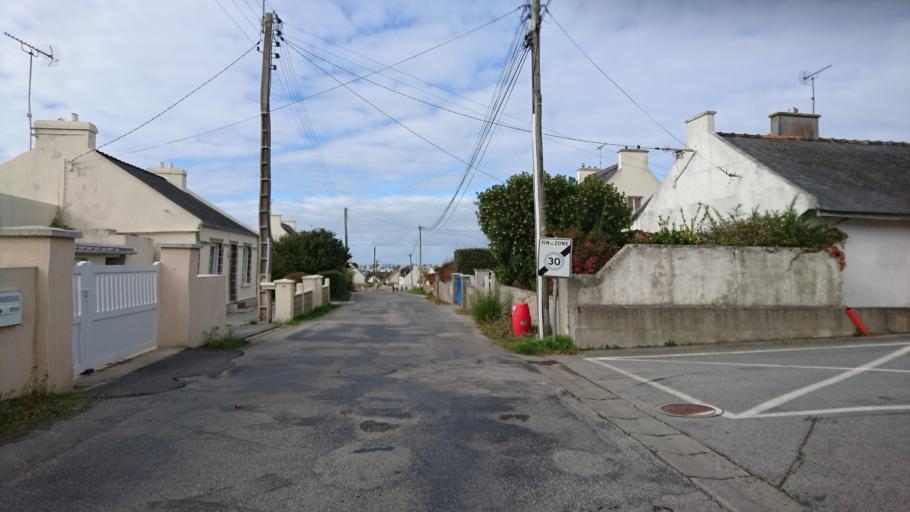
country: FR
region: Brittany
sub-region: Departement du Finistere
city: Lampaul-Plouarzel
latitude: 48.4469
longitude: -4.7626
